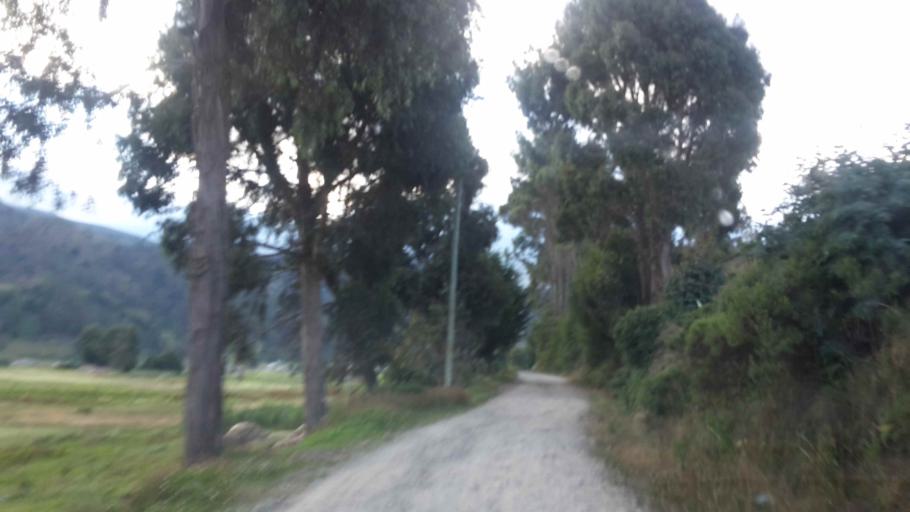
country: BO
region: Cochabamba
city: Colomi
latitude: -17.2782
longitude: -65.9124
